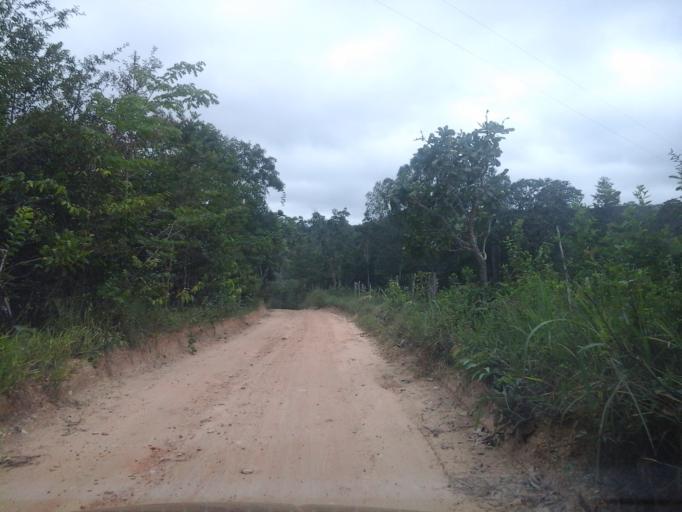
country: BR
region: Goias
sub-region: Pirenopolis
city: Pirenopolis
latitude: -15.7468
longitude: -49.0435
